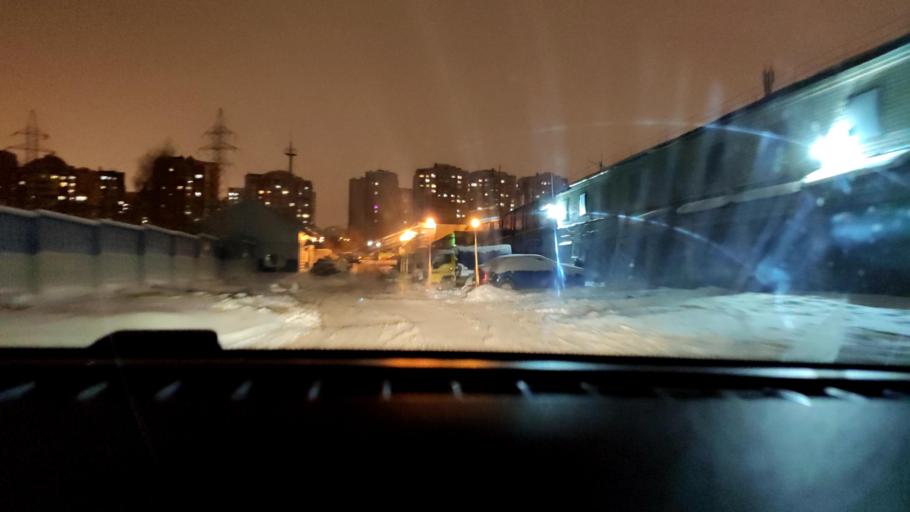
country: RU
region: Samara
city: Samara
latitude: 53.2470
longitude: 50.1828
